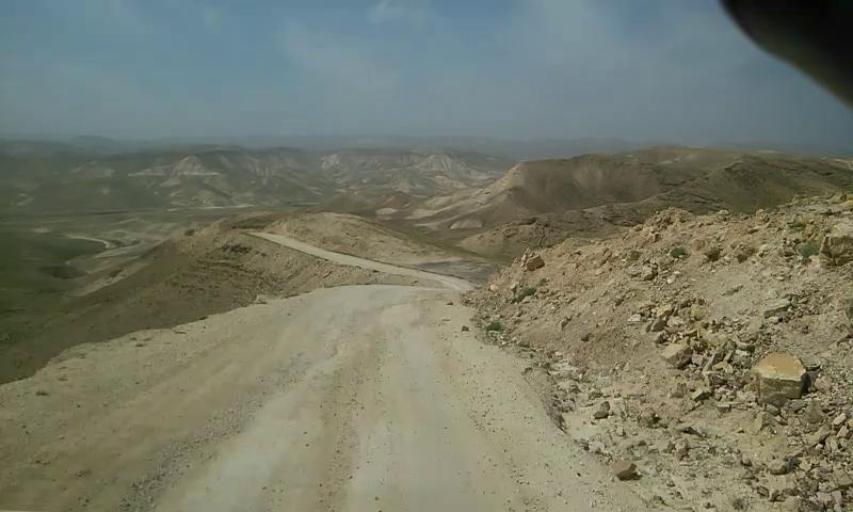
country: PS
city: `Arab ar Rashaydah
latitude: 31.5164
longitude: 35.2912
